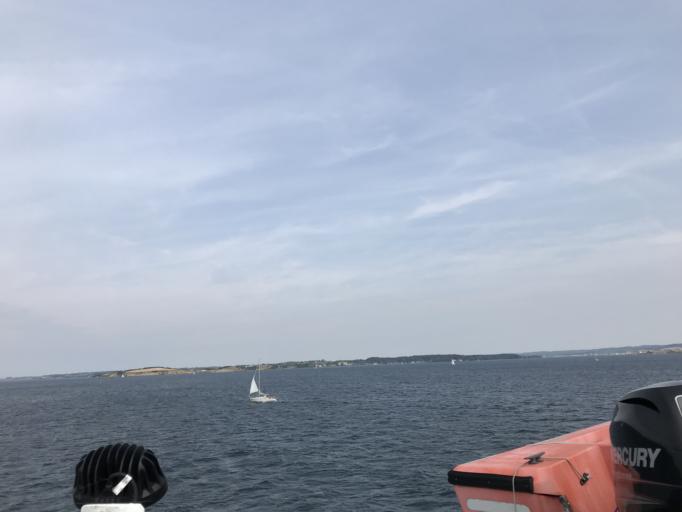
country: DK
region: South Denmark
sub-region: Faaborg-Midtfyn Kommune
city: Faaborg
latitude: 55.0435
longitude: 10.2323
